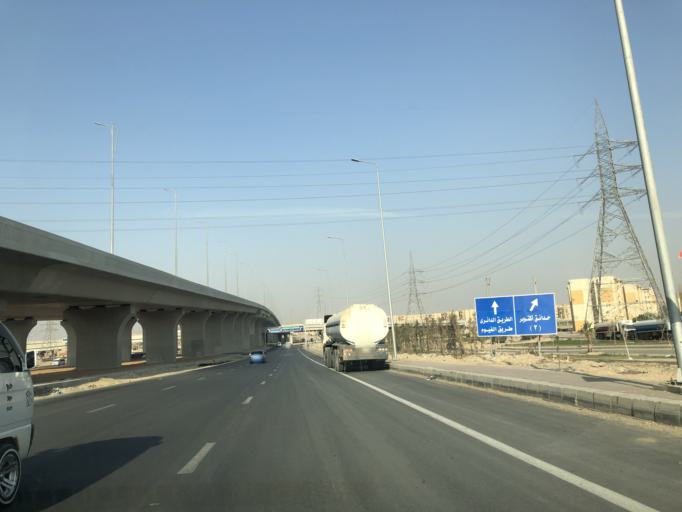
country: EG
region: Al Jizah
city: Madinat Sittah Uktubar
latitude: 29.9093
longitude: 30.9280
